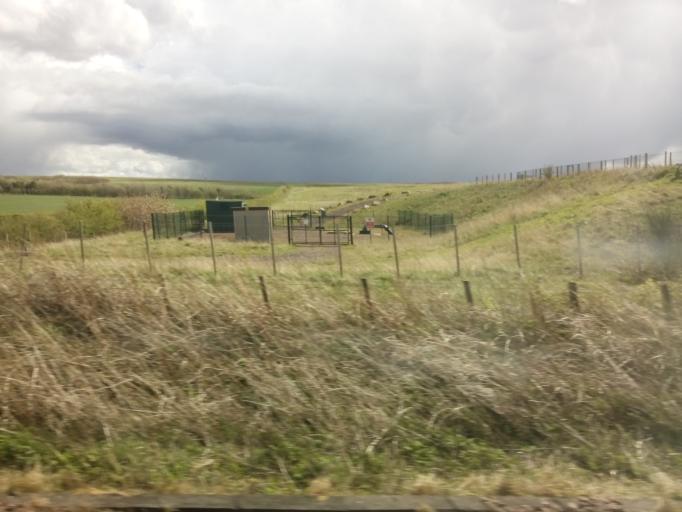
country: GB
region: Scotland
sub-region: East Lothian
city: Tranent
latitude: 55.9632
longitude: -2.9349
